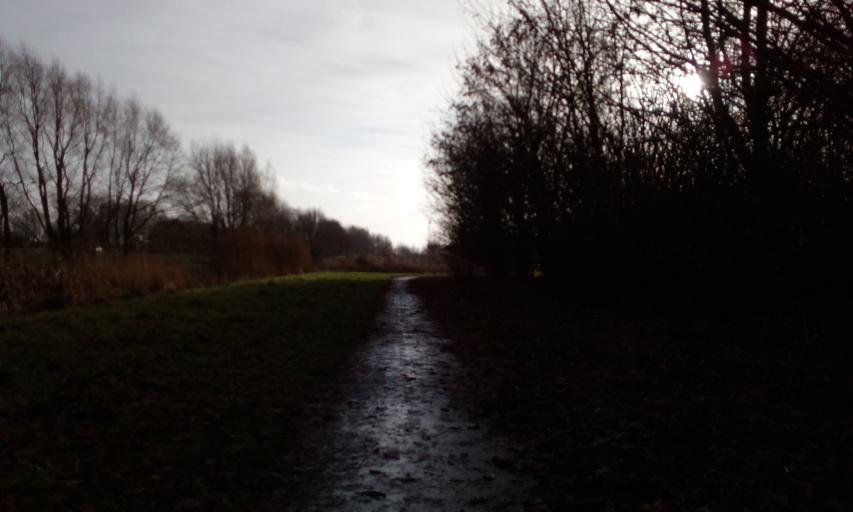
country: NL
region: South Holland
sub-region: Gemeente Lansingerland
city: Berkel en Rodenrijs
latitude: 51.9713
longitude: 4.4828
